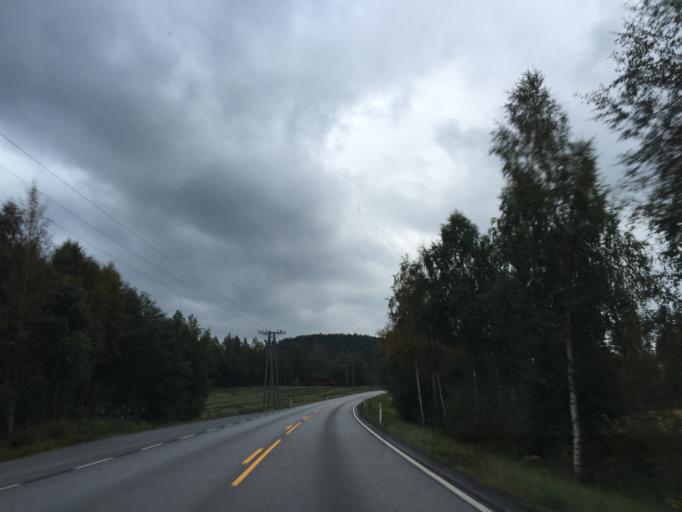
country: NO
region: Hedmark
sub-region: Nord-Odal
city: Sand
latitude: 60.4354
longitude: 11.5096
